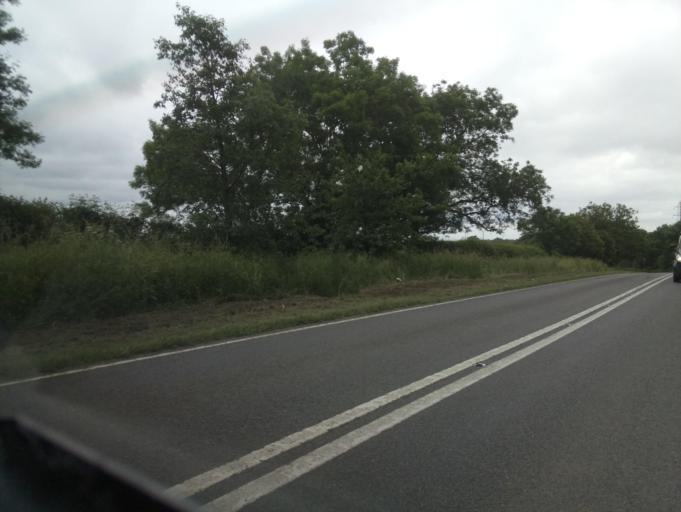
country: GB
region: England
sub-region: Leicestershire
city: Sileby
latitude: 52.8068
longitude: -1.0765
